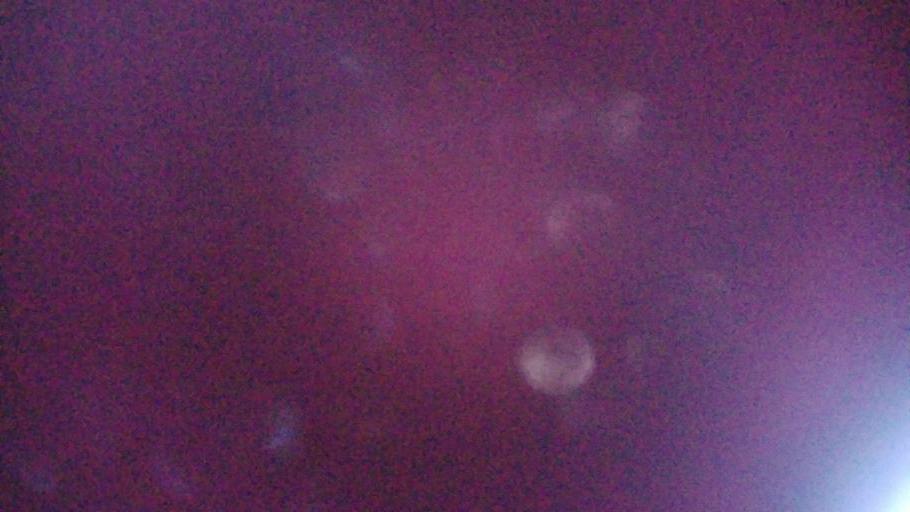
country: US
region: Florida
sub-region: Lee County
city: Olga
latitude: 26.7783
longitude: -81.7415
